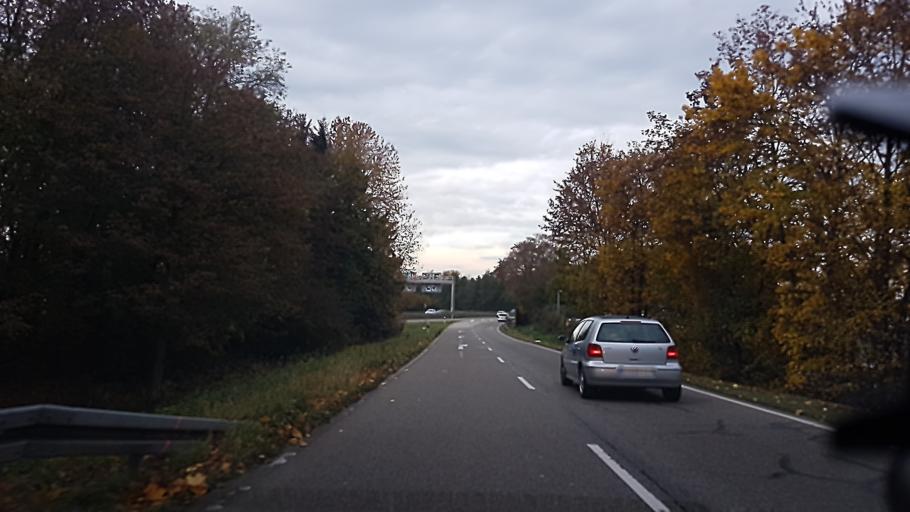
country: DE
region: Baden-Wuerttemberg
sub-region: Freiburg Region
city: Gundelfingen
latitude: 48.0367
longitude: 7.8617
